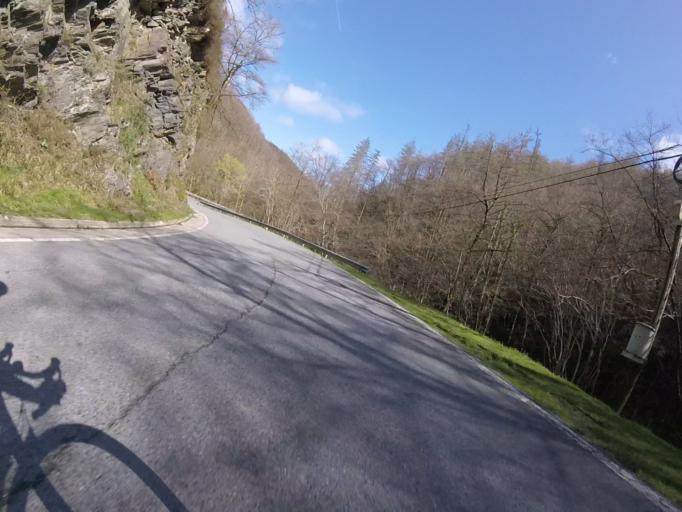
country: ES
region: Navarre
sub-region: Provincia de Navarra
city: Ezkurra
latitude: 43.0973
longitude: -1.8645
